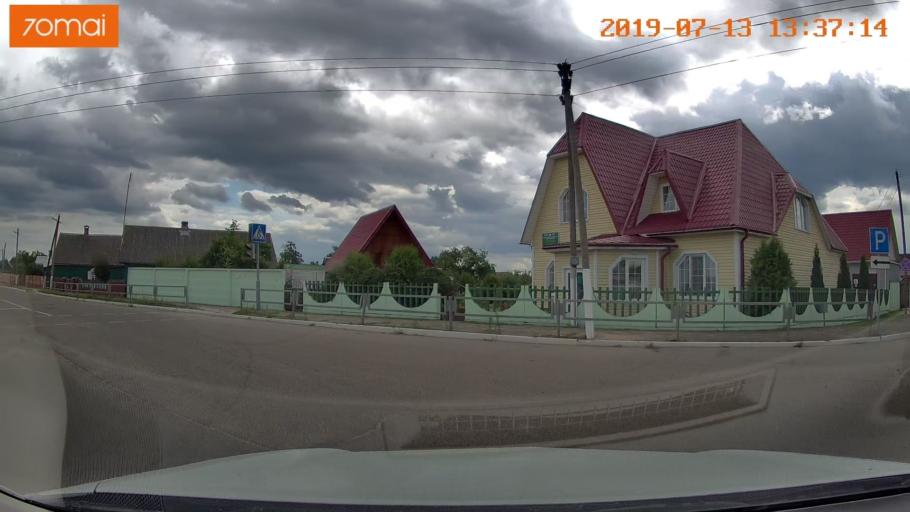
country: BY
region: Mogilev
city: Asipovichy
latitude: 53.3012
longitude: 28.6240
